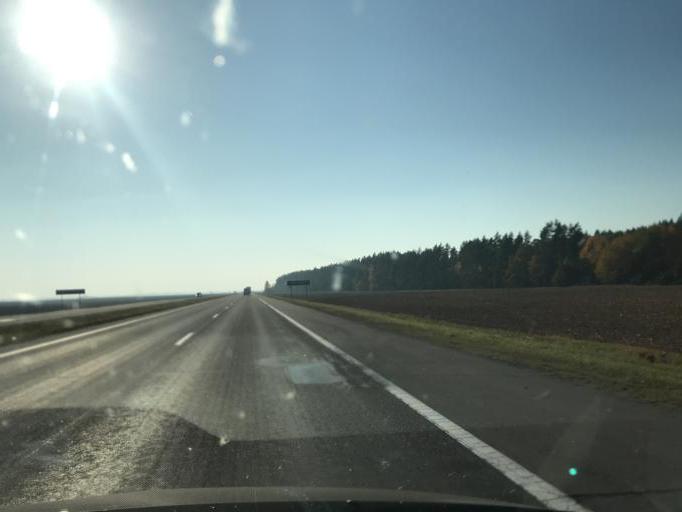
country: BY
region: Minsk
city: Haradzyeya
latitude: 53.3717
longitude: 26.4938
